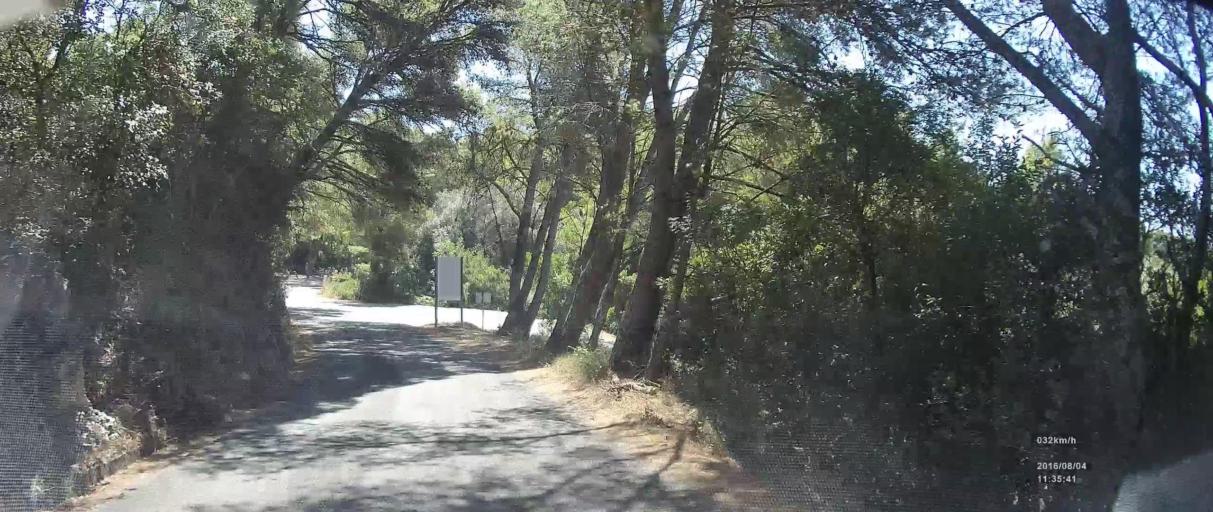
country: HR
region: Dubrovacko-Neretvanska
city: Blato
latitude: 42.7791
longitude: 17.3669
